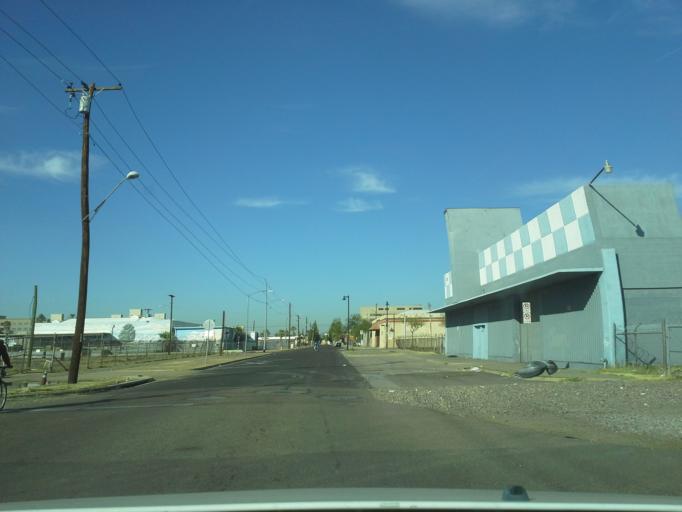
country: US
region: Arizona
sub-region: Maricopa County
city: Phoenix
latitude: 33.4440
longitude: -112.0847
